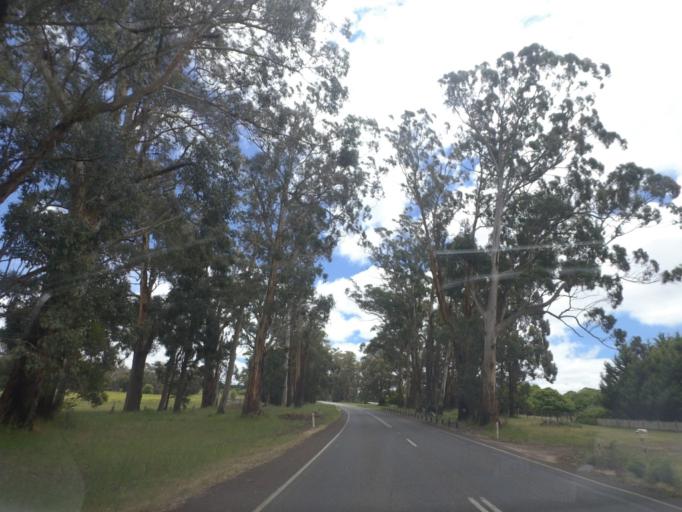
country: AU
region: Victoria
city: Brown Hill
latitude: -37.4621
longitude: 144.1423
